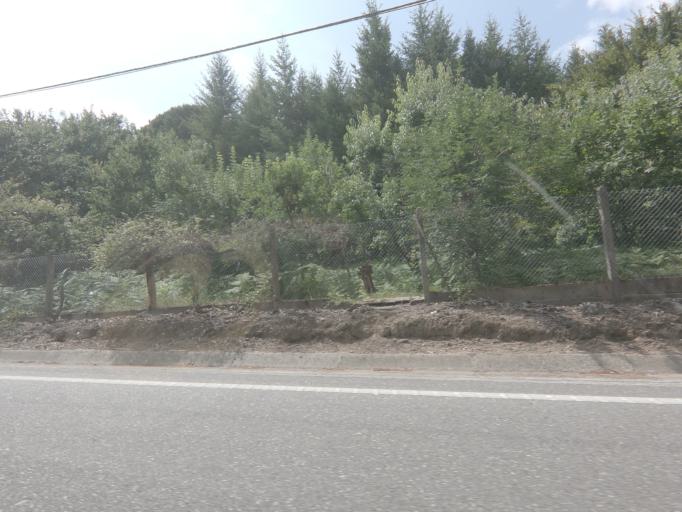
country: PT
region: Viana do Castelo
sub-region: Valenca
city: Valenca
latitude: 42.0281
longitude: -8.6756
